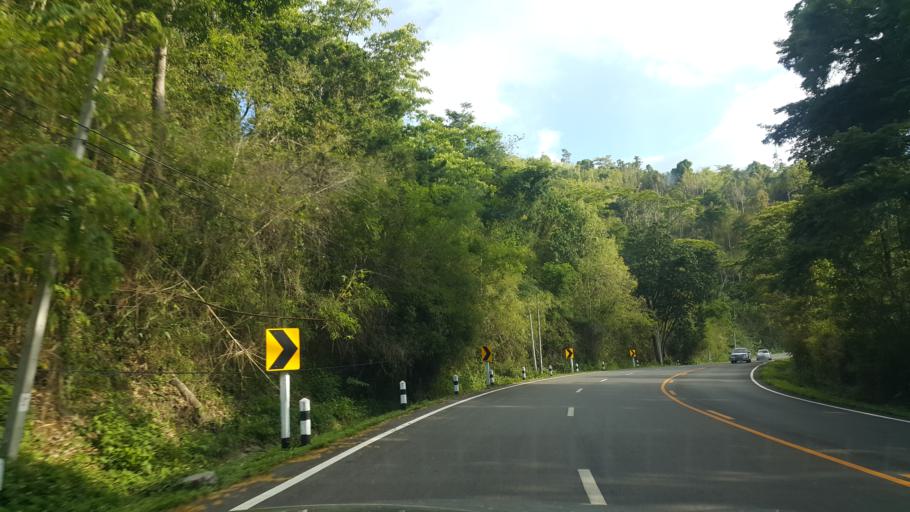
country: TH
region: Phayao
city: Phayao
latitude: 19.0594
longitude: 99.7916
